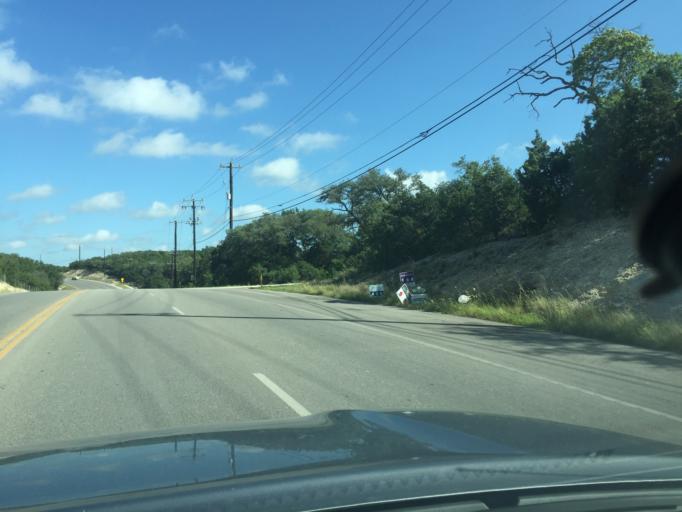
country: US
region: Texas
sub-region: Bexar County
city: Timberwood Park
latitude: 29.7115
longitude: -98.4501
